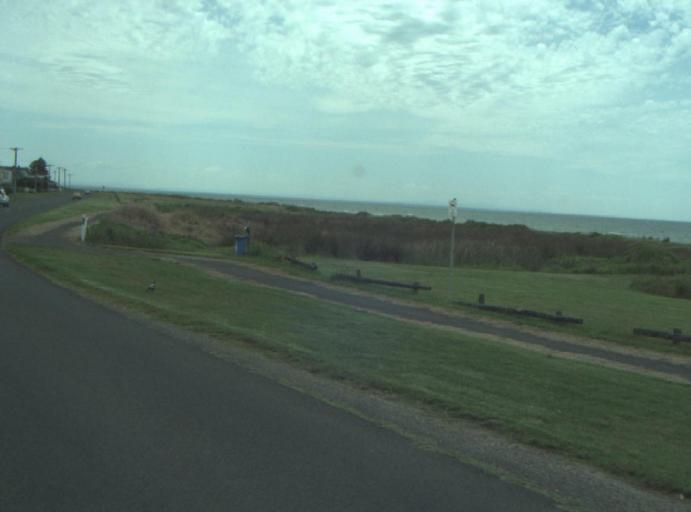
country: AU
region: Victoria
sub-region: Greater Geelong
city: Clifton Springs
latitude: -38.1265
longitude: 144.6968
